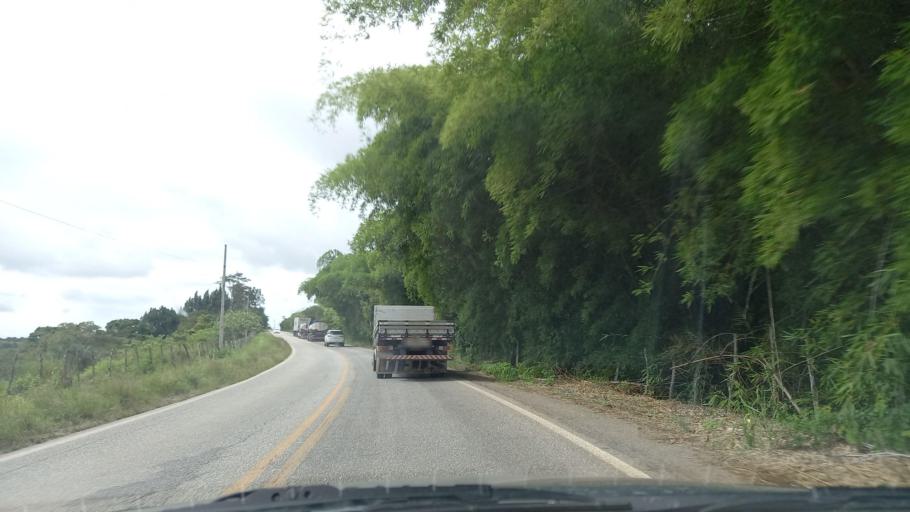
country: BR
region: Pernambuco
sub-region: Canhotinho
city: Canhotinho
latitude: -8.8637
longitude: -36.1827
